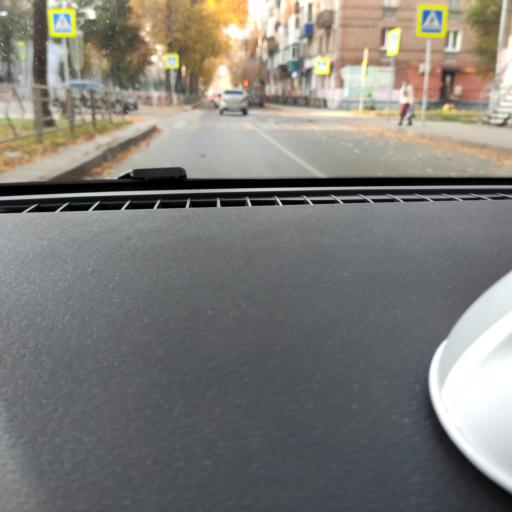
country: RU
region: Samara
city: Petra-Dubrava
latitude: 53.2381
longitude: 50.2790
